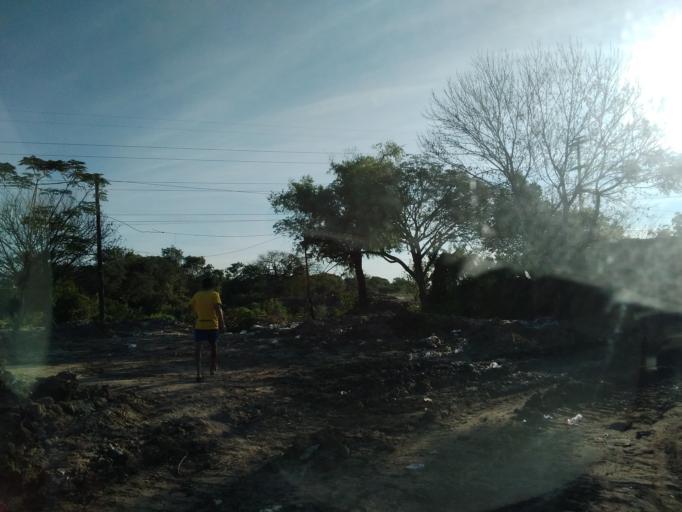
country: AR
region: Corrientes
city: Corrientes
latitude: -27.5041
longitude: -58.8360
